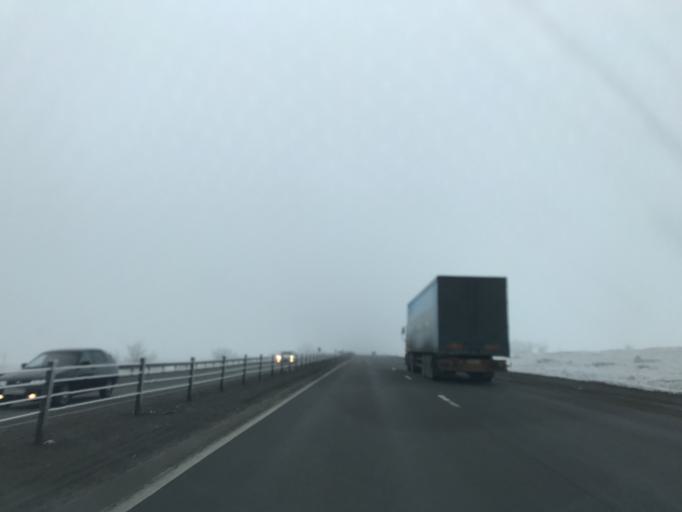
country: RU
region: Rostov
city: Likhoy
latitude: 48.1521
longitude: 40.2611
